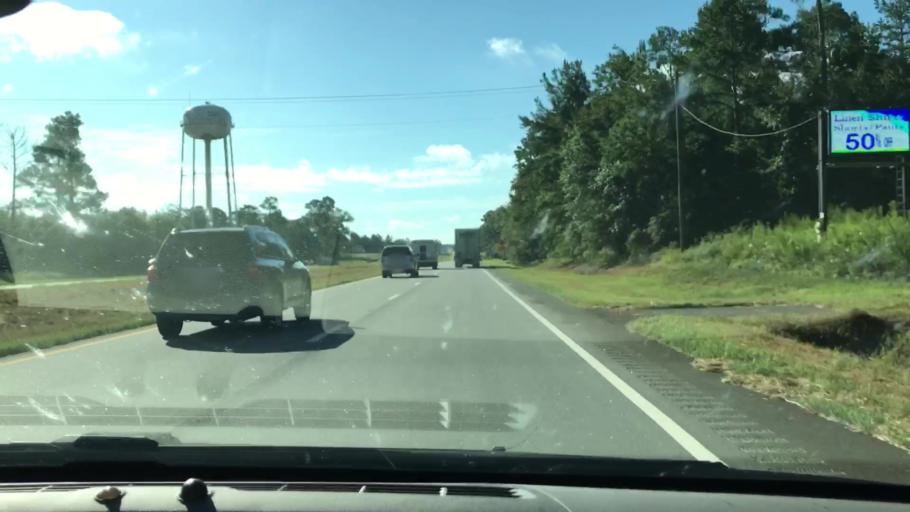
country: US
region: Georgia
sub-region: Dougherty County
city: Albany
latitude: 31.6416
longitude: -84.2535
